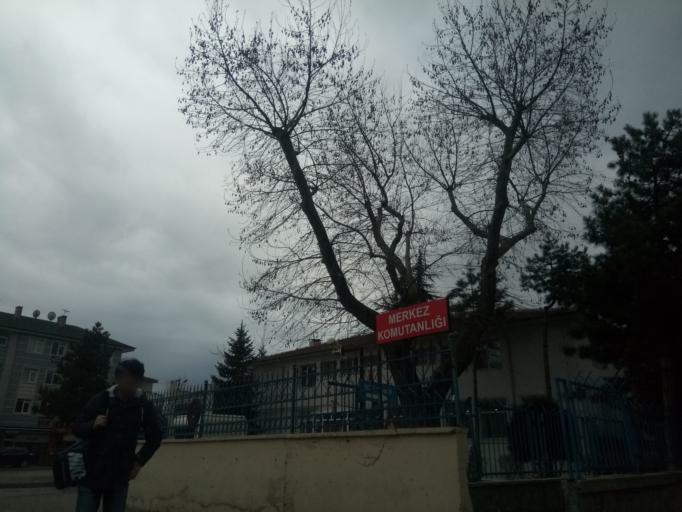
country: TR
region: Bolu
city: Bolu
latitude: 40.7036
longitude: 31.5712
